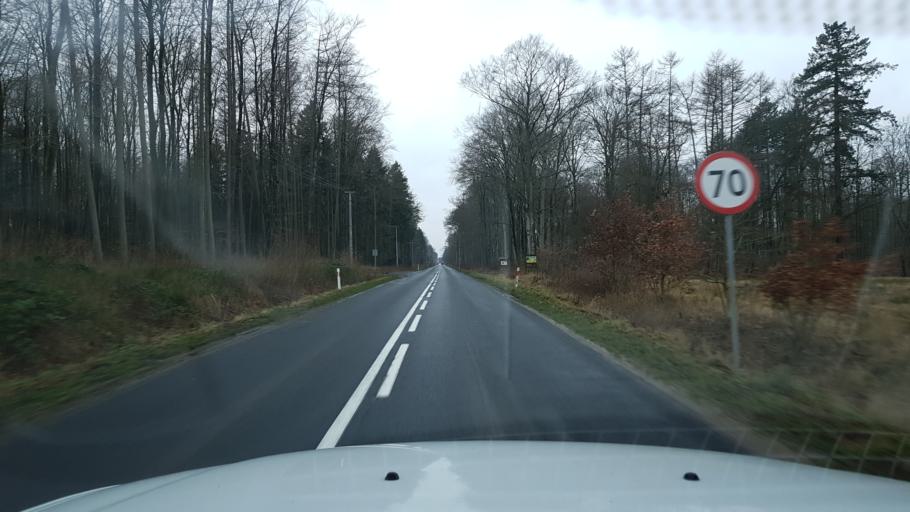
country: PL
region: West Pomeranian Voivodeship
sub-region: Powiat gryficki
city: Trzebiatow
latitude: 54.0552
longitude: 15.3604
